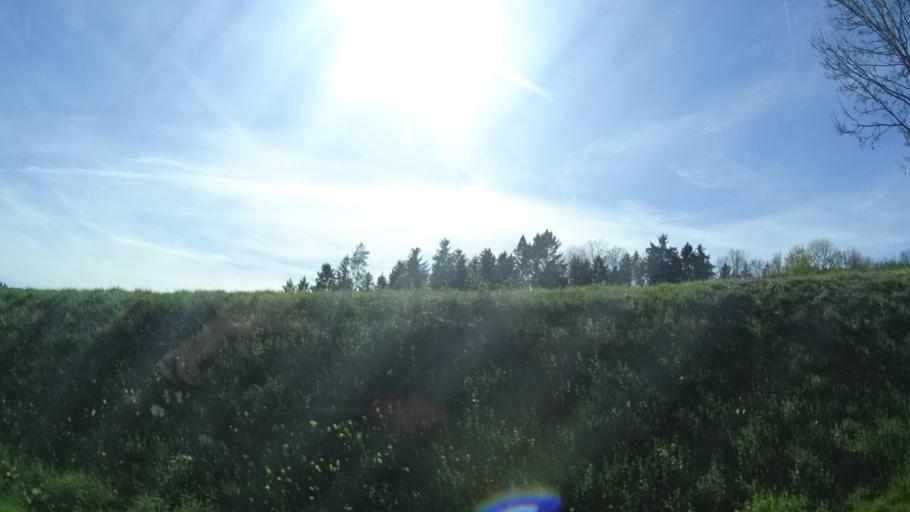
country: DE
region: Bavaria
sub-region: Regierungsbezirk Unterfranken
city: Burgpreppach
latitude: 50.1066
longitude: 10.6434
